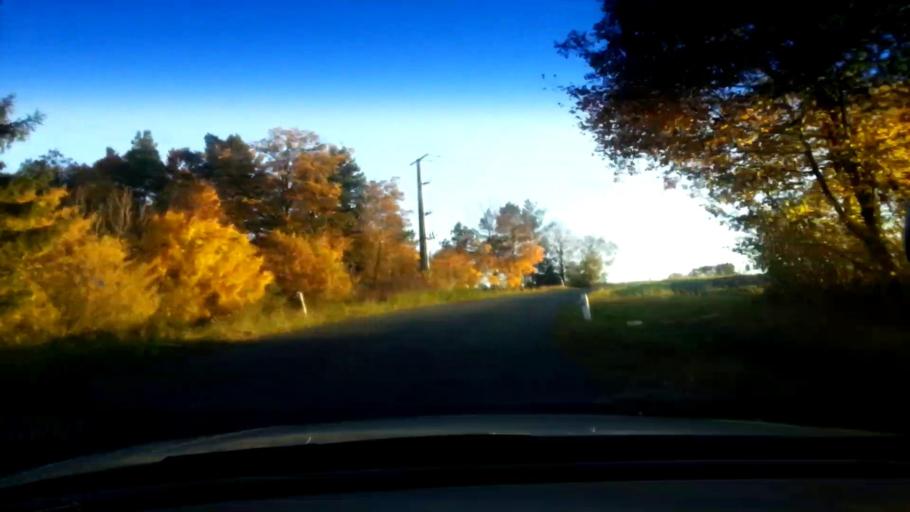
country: DE
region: Bavaria
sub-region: Upper Franconia
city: Heiligenstadt
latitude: 49.8450
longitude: 11.1843
